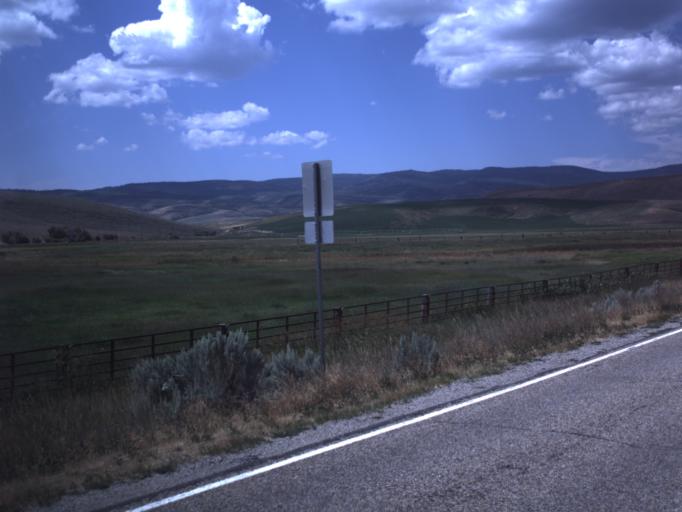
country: US
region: Utah
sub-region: Rich County
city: Randolph
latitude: 41.8410
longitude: -111.3440
